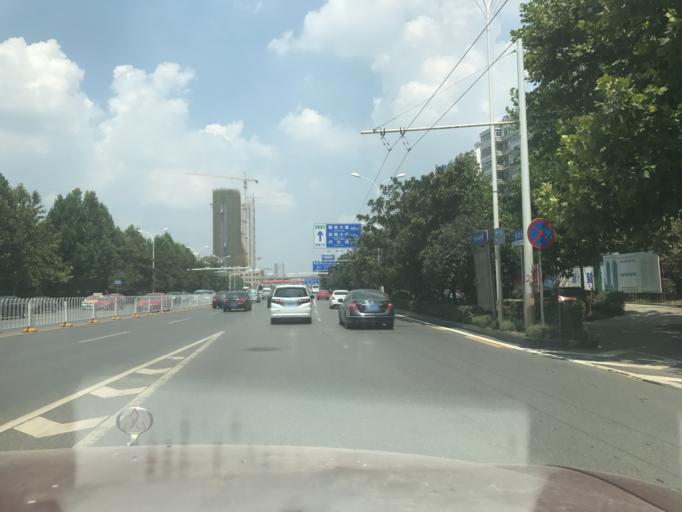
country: CN
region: Hubei
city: Jiang'an
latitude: 30.6176
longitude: 114.3001
